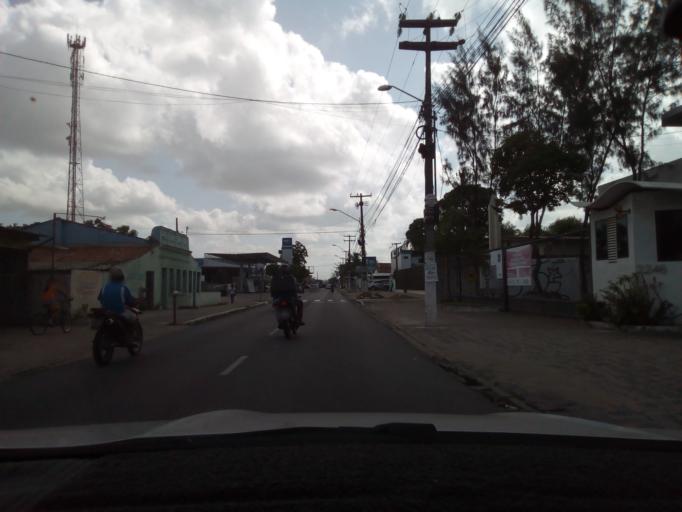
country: BR
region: Paraiba
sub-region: Bayeux
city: Bayeux
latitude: -7.1223
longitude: -34.9137
